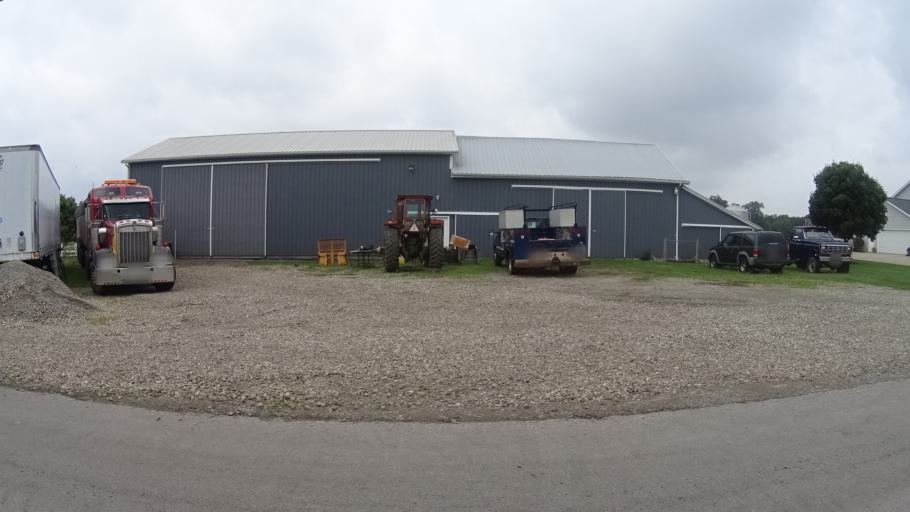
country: US
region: Ohio
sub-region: Huron County
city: Bellevue
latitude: 41.3524
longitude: -82.7730
